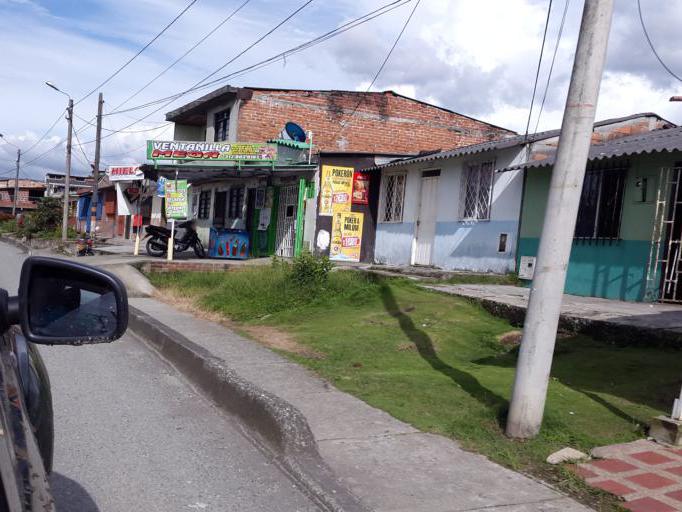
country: CO
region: Quindio
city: Cordoba
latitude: 4.4285
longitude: -75.7189
